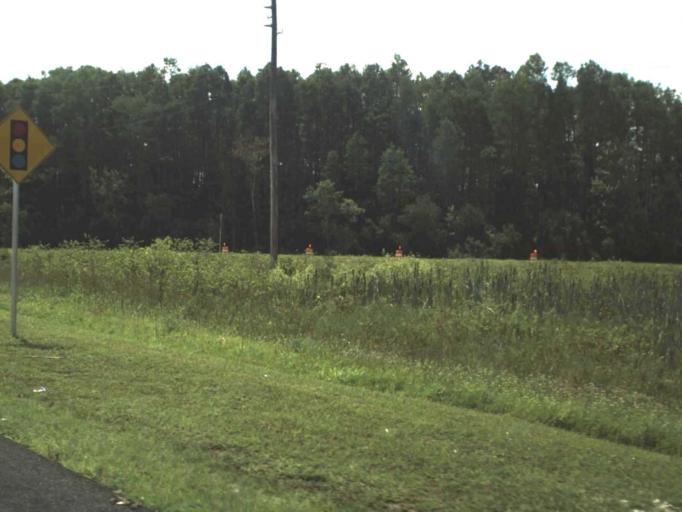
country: US
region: Florida
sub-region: Volusia County
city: Glencoe
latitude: 29.0126
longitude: -80.9895
